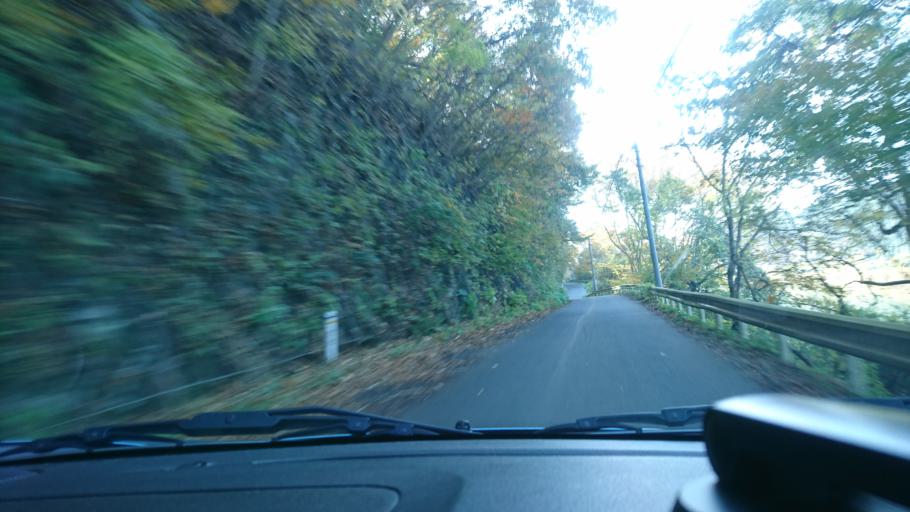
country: JP
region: Iwate
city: Ichinoseki
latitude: 38.8103
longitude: 141.2514
